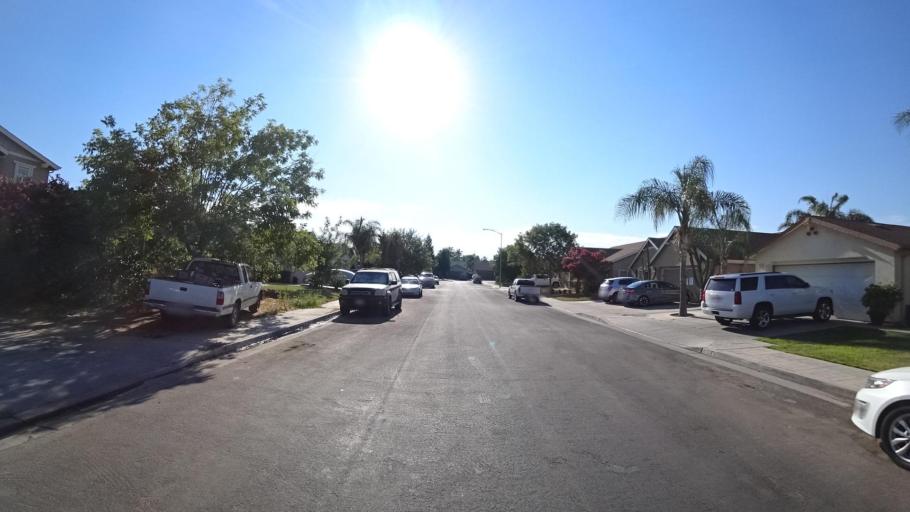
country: US
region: California
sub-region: Fresno County
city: Fresno
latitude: 36.7131
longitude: -119.7473
